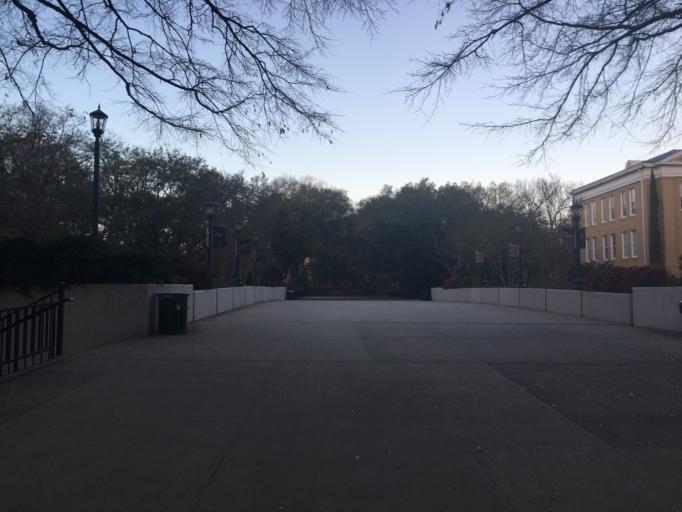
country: US
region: South Carolina
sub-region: Richland County
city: Columbia
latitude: 33.9992
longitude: -81.0251
